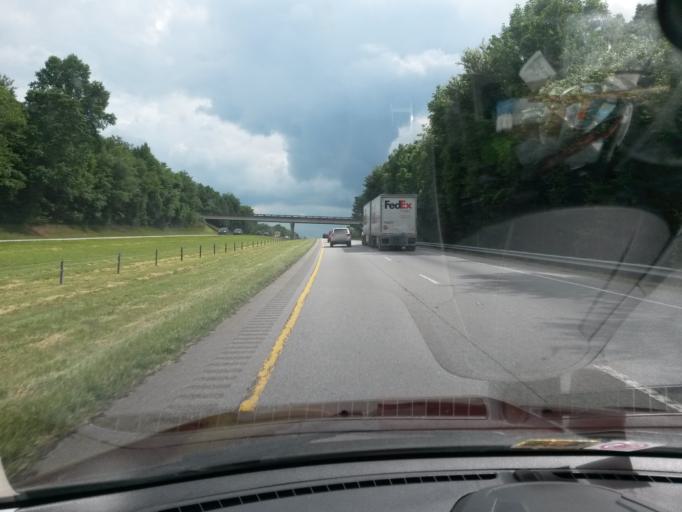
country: US
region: North Carolina
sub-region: Iredell County
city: Statesville
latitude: 35.9612
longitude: -80.8467
